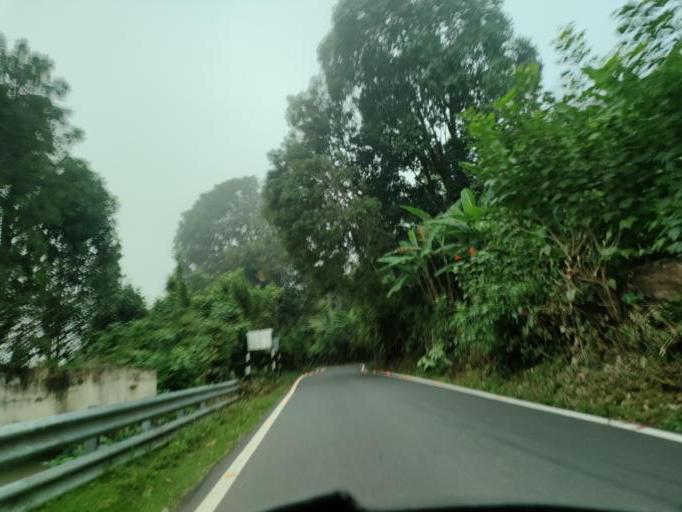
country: IN
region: Tamil Nadu
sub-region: Dindigul
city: Ayakudi
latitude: 10.3349
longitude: 77.5621
